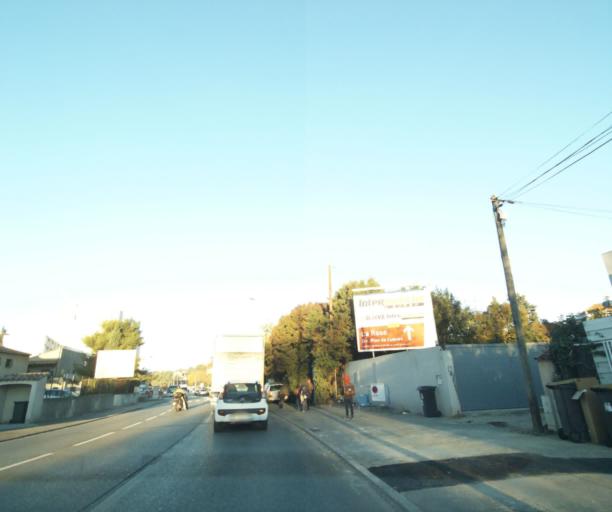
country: FR
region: Provence-Alpes-Cote d'Azur
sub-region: Departement des Bouches-du-Rhone
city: Marseille 13
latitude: 43.3279
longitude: 5.4354
